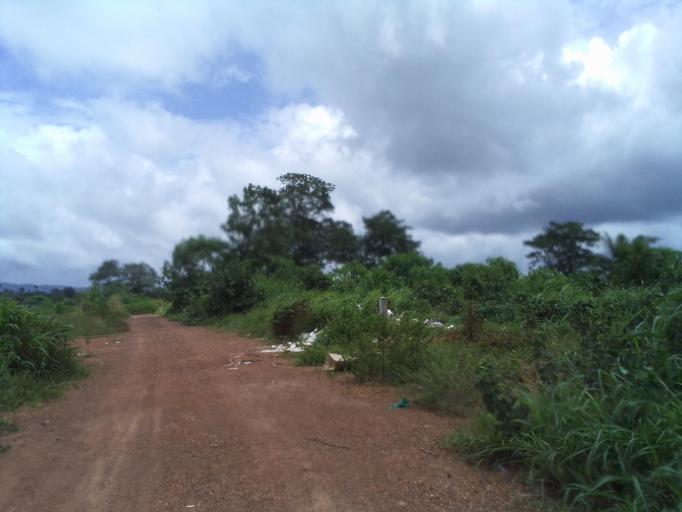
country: SL
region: Eastern Province
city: Kenema
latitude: 7.8207
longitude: -11.1813
